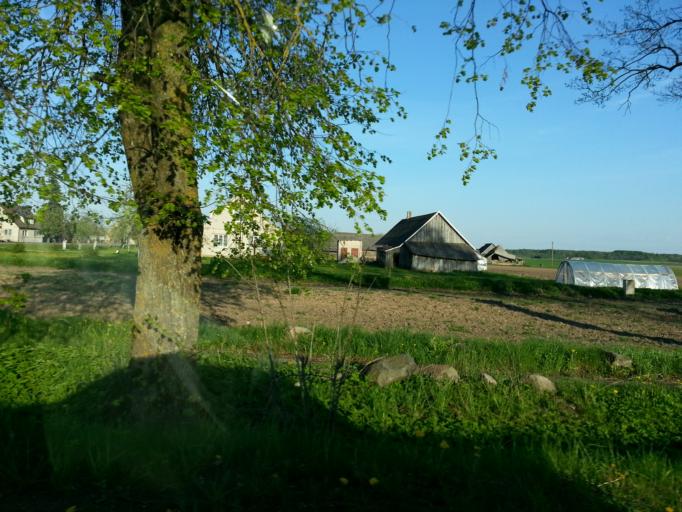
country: LT
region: Vilnius County
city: Ukmerge
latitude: 55.4273
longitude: 24.5898
